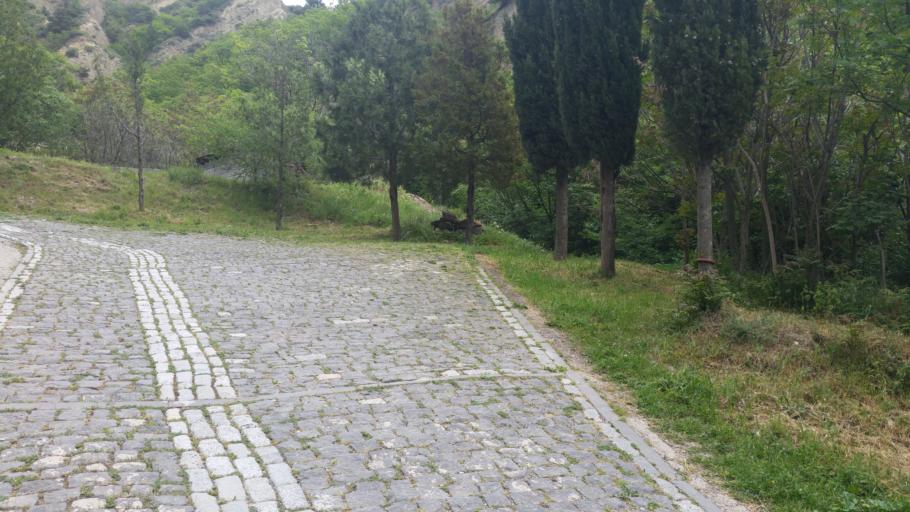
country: GE
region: Mtskheta-Mtianeti
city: Mtskheta
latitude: 41.8622
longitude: 44.6409
